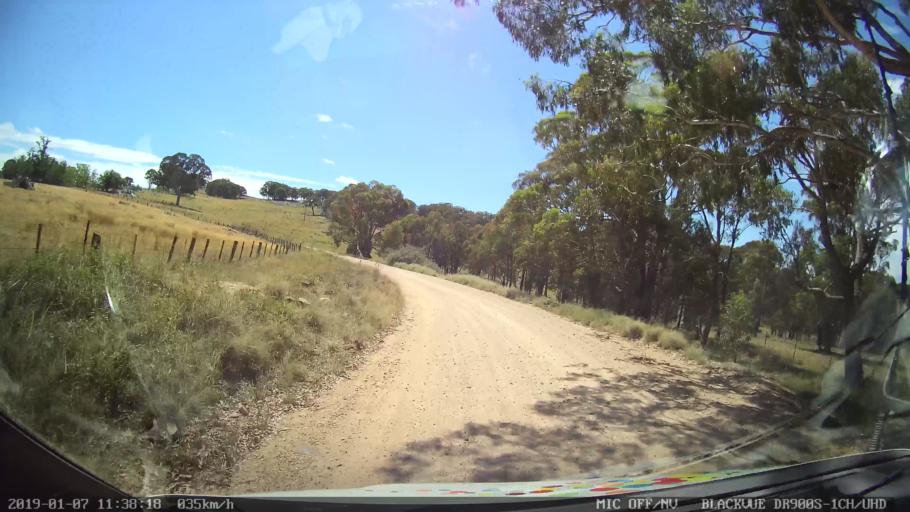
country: AU
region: New South Wales
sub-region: Armidale Dumaresq
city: Armidale
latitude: -30.3714
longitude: 151.5714
